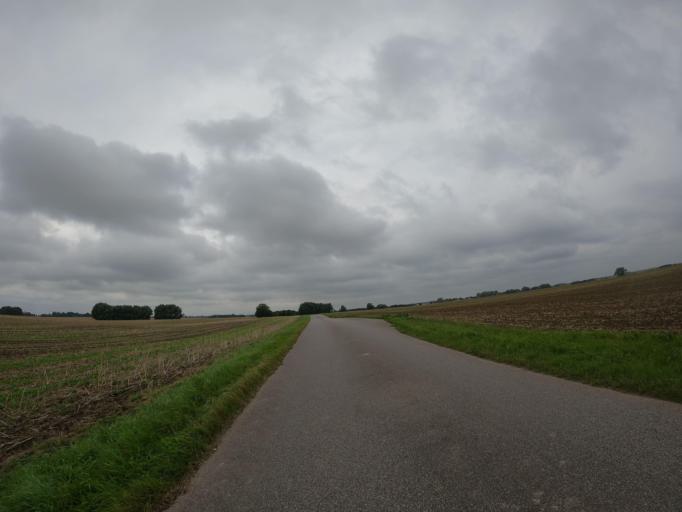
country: DE
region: Mecklenburg-Vorpommern
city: Garz
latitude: 54.2937
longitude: 13.3241
